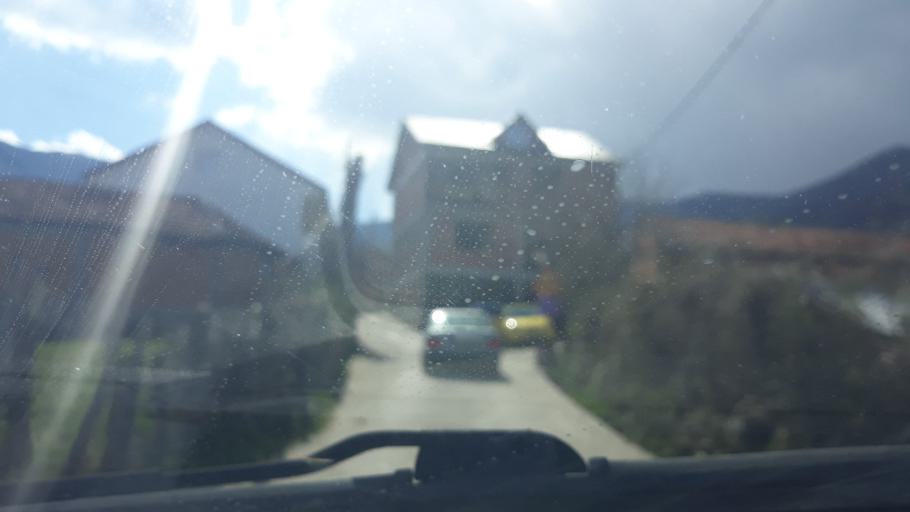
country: MK
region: Caska
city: Caska
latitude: 41.6430
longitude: 21.5926
